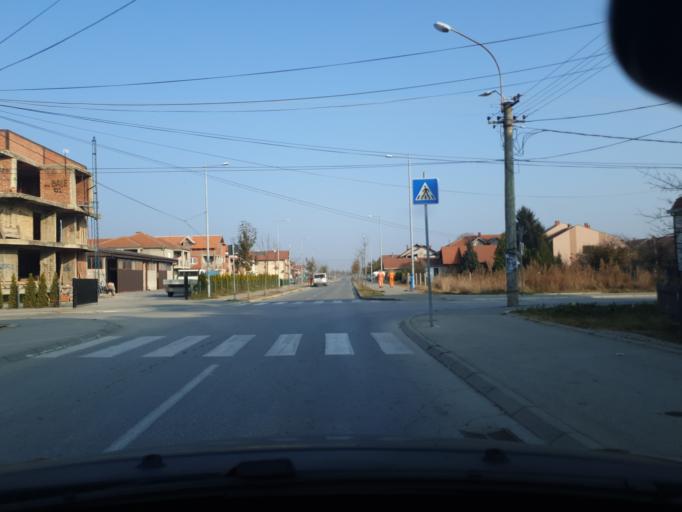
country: RS
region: Central Serbia
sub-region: Jablanicki Okrug
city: Leskovac
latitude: 42.9988
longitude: 21.9237
